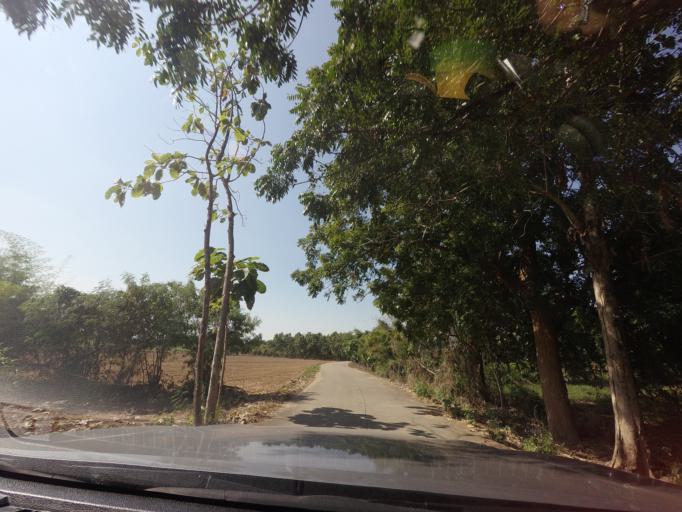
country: TH
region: Sukhothai
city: Sawankhalok
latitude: 17.3227
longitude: 99.8240
